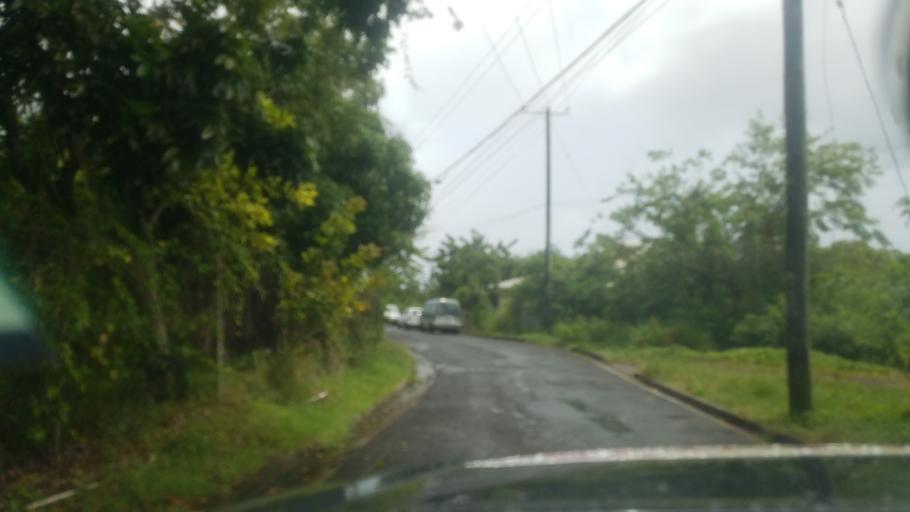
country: LC
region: Laborie Quarter
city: Laborie
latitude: 13.7554
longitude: -60.9757
